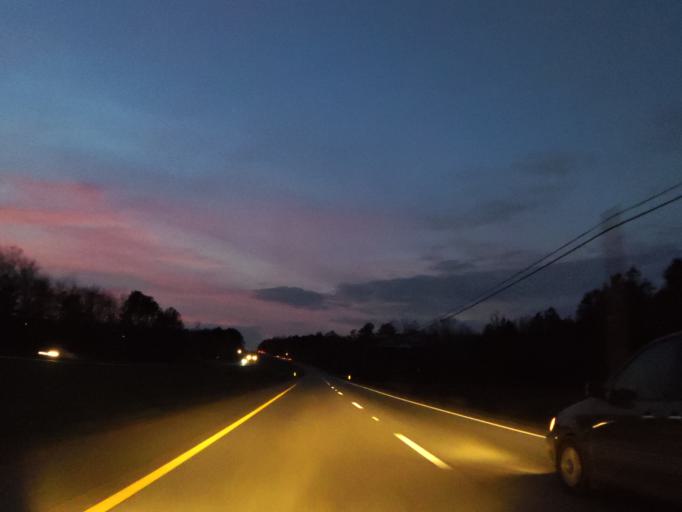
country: US
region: Tennessee
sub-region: Polk County
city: Benton
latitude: 35.1330
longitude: -84.7475
